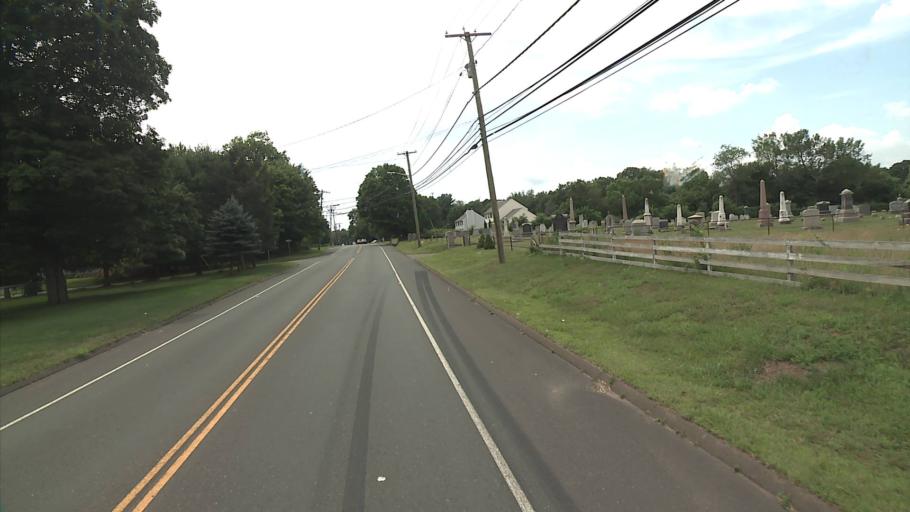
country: US
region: Connecticut
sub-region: New Haven County
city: North Branford
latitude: 41.3297
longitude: -72.8095
